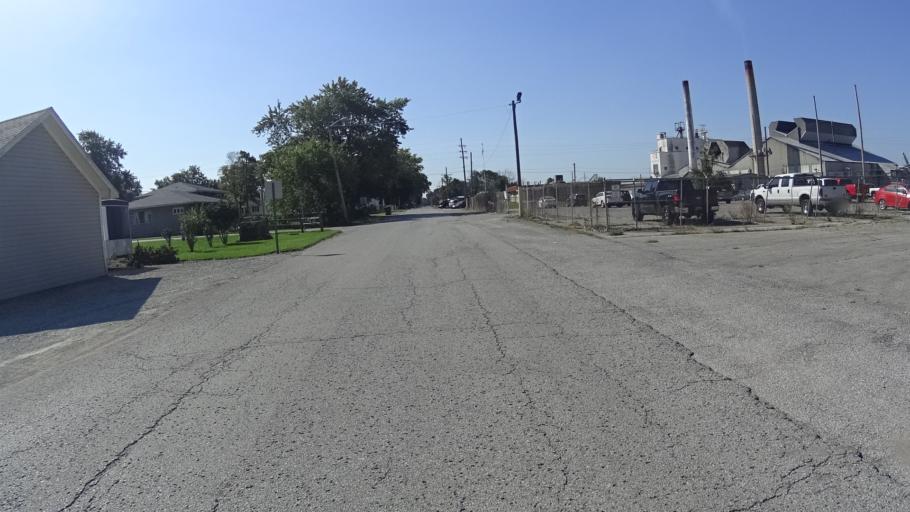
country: US
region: Indiana
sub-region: Madison County
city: Lapel
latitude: 40.0689
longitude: -85.8536
